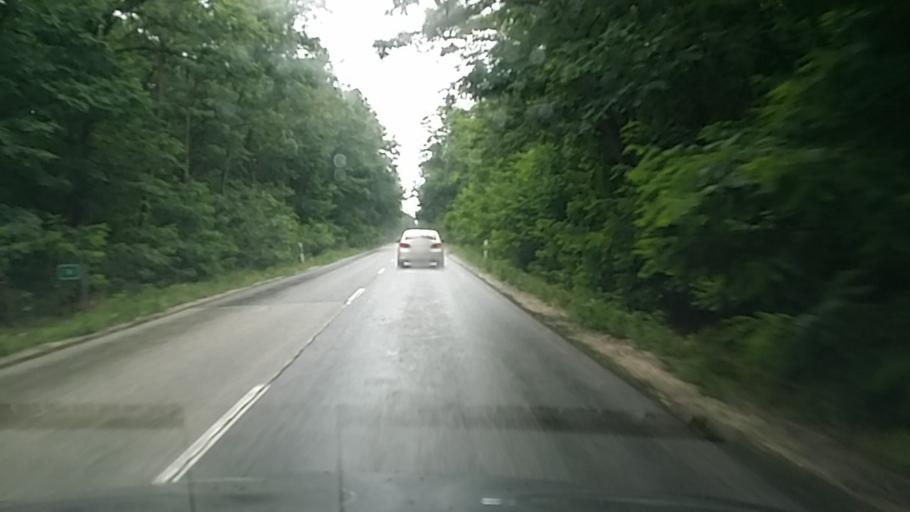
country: HU
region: Pest
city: Ullo
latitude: 47.3458
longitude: 19.3144
